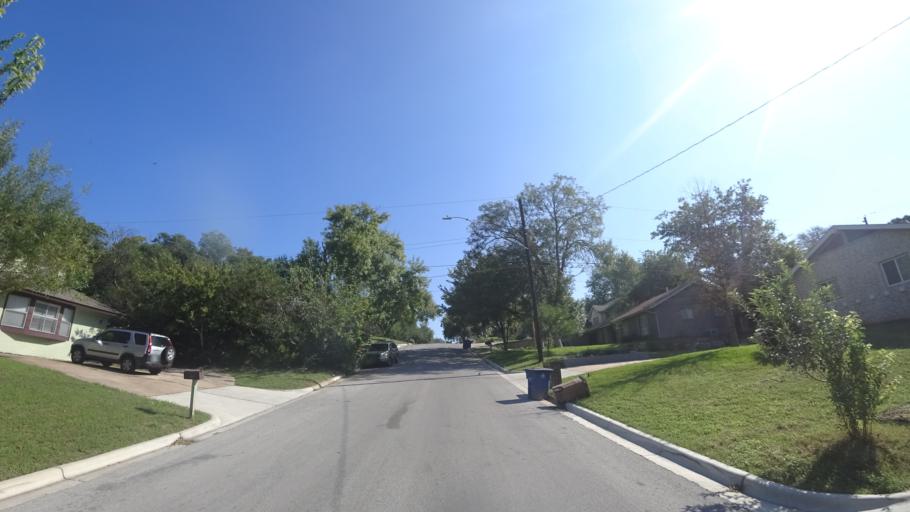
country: US
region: Texas
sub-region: Travis County
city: Austin
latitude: 30.3127
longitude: -97.6680
